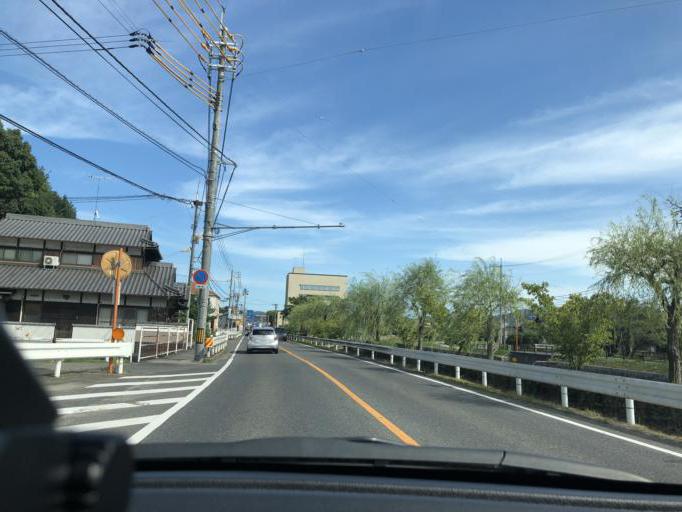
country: JP
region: Okayama
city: Kurashiki
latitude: 34.5850
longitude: 133.7787
